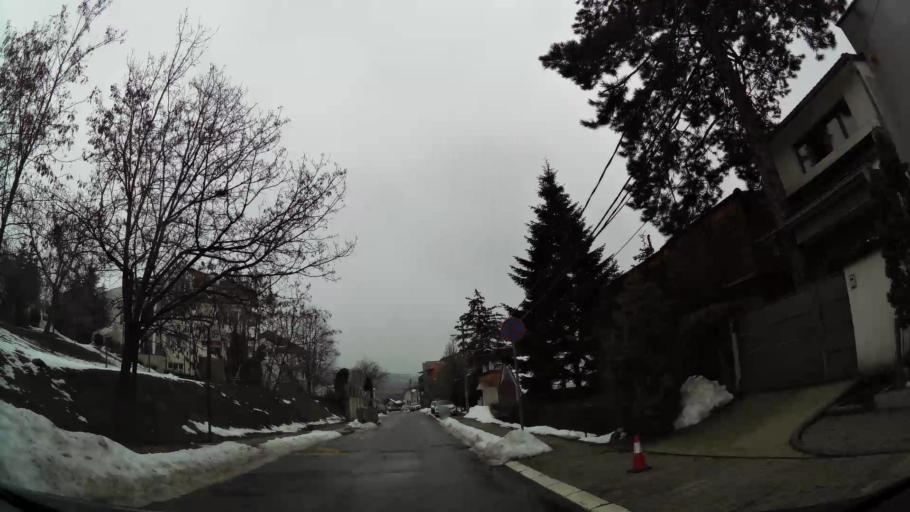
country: RS
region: Central Serbia
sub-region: Belgrade
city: Rakovica
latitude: 44.7580
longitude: 20.4515
